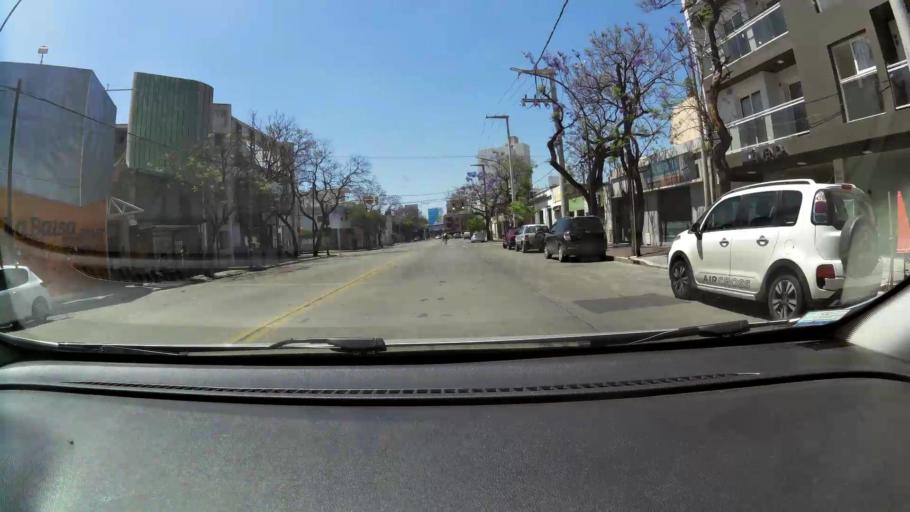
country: AR
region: Cordoba
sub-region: Departamento de Capital
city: Cordoba
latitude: -31.4020
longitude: -64.1980
